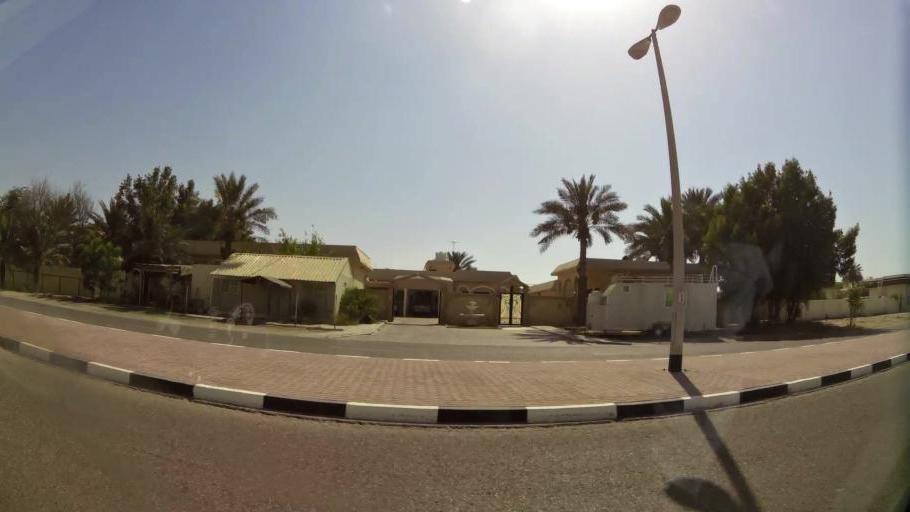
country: AE
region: Ajman
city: Ajman
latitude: 25.4148
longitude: 55.4691
